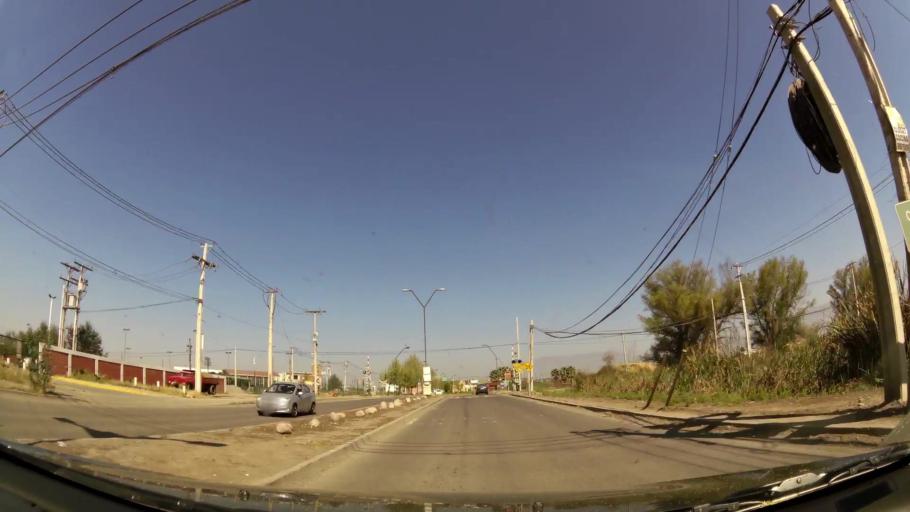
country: CL
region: Santiago Metropolitan
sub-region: Provincia de Chacabuco
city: Chicureo Abajo
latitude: -33.3234
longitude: -70.7405
